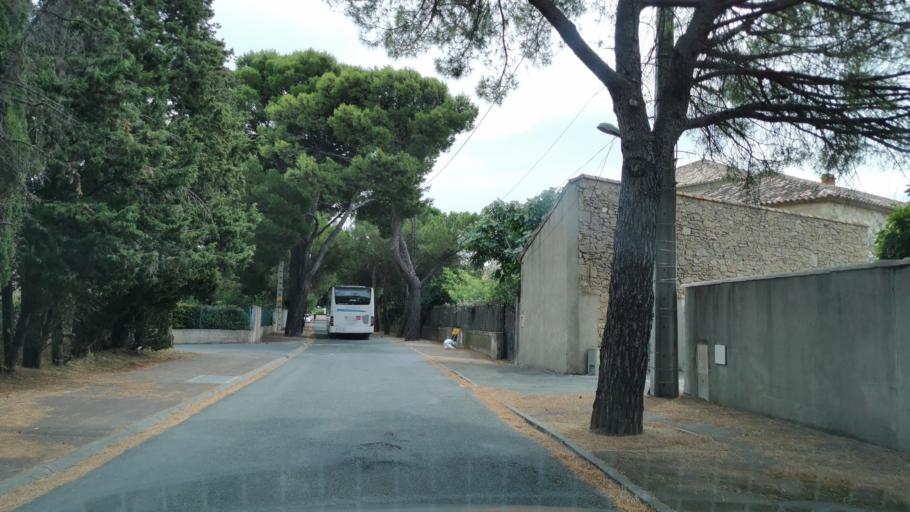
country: FR
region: Languedoc-Roussillon
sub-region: Departement de l'Aude
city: Argeliers
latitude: 43.3077
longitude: 2.9150
